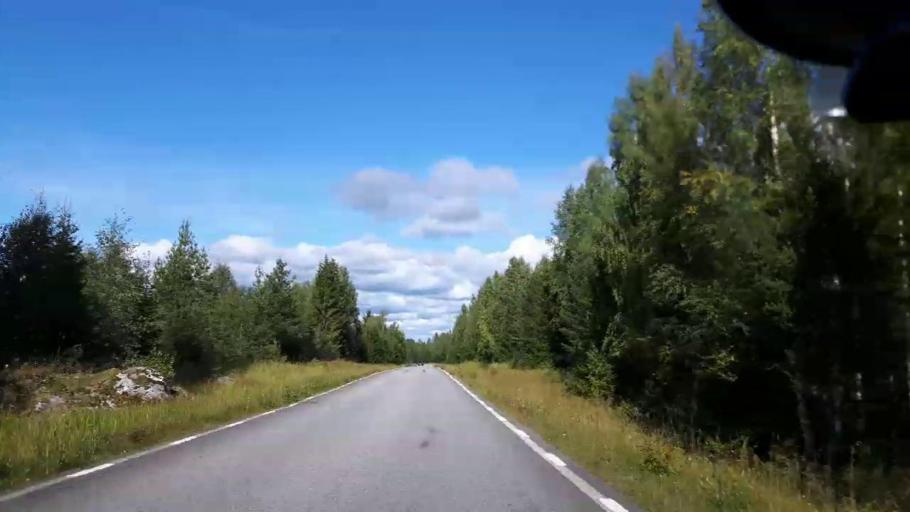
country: SE
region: Jaemtland
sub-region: OEstersunds Kommun
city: Brunflo
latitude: 63.2117
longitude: 15.2484
